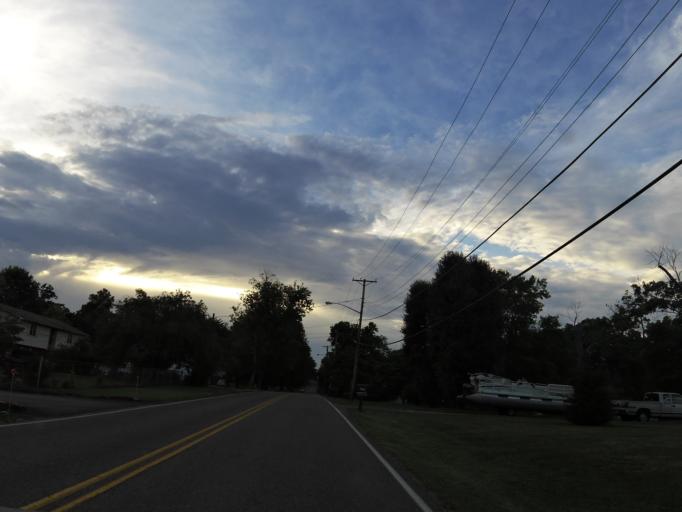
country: US
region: Tennessee
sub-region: Knox County
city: Knoxville
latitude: 36.0373
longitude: -83.9068
